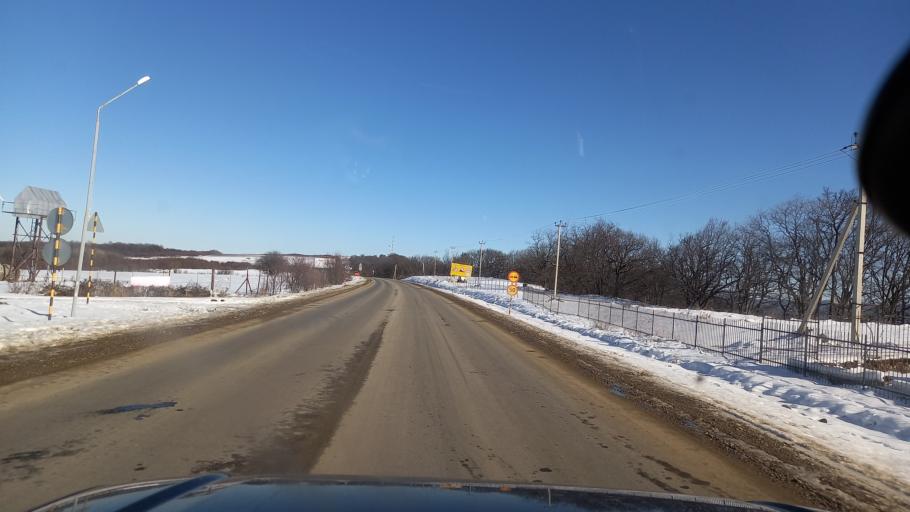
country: RU
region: Adygeya
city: Kamennomostskiy
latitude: 44.2338
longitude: 40.1481
